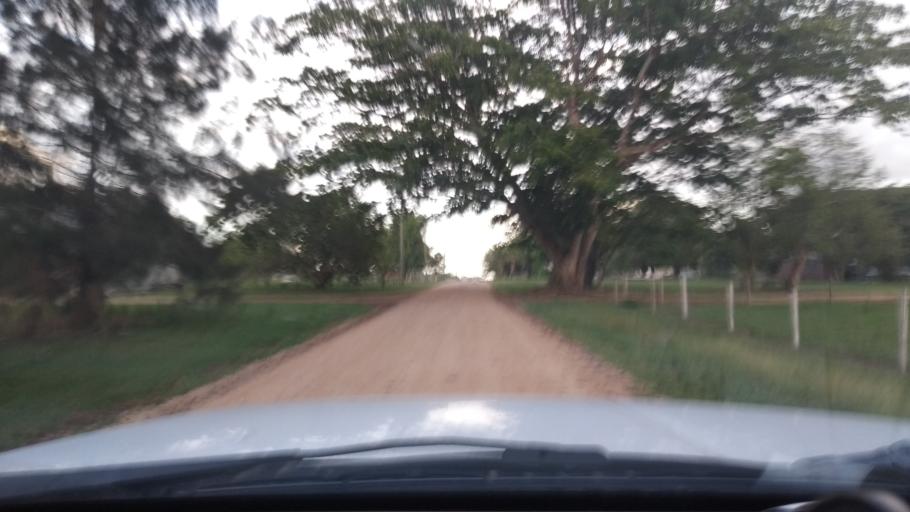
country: BZ
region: Cayo
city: San Ignacio
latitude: 17.2240
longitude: -88.9977
